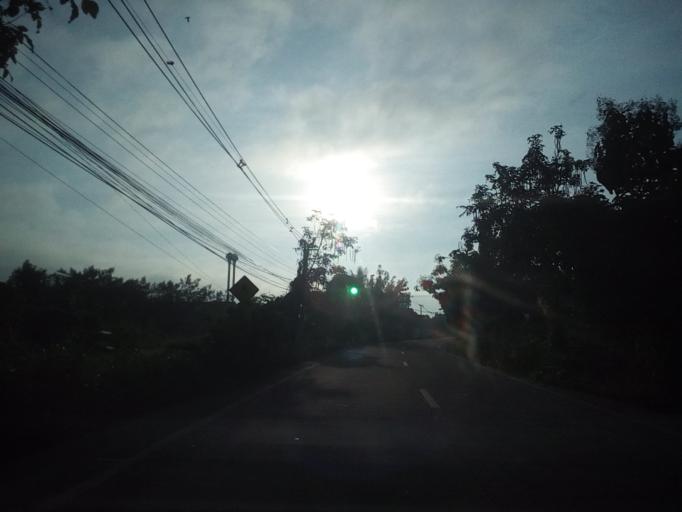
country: TH
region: Lamphun
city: Ban Thi
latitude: 18.6274
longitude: 99.0702
